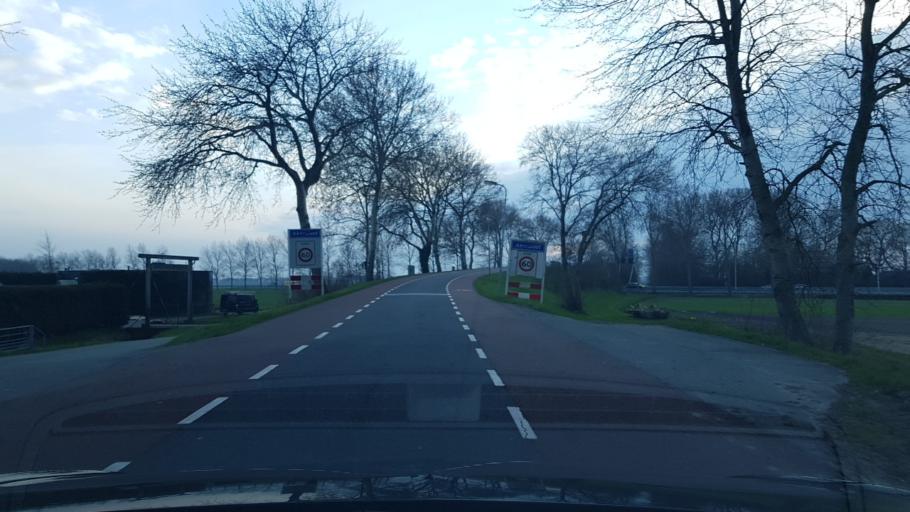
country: NL
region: North Holland
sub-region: Gemeente Uitgeest
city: Uitgeest
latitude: 52.5530
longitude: 4.7216
